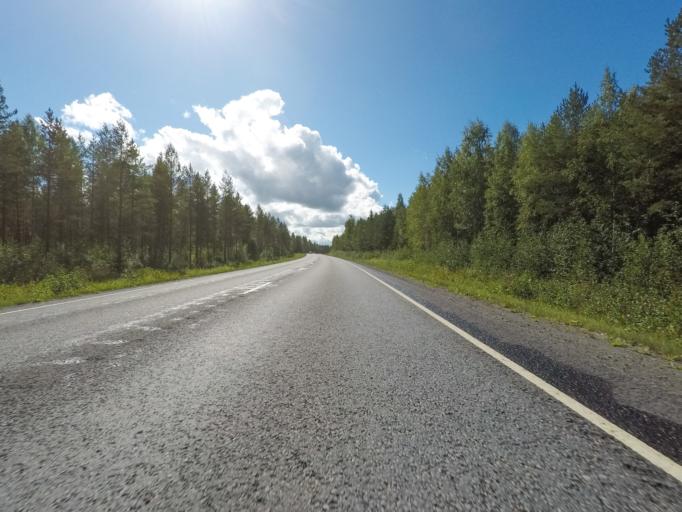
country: FI
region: Central Finland
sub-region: Jyvaeskylae
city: Hankasalmi
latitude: 62.3501
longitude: 26.5589
